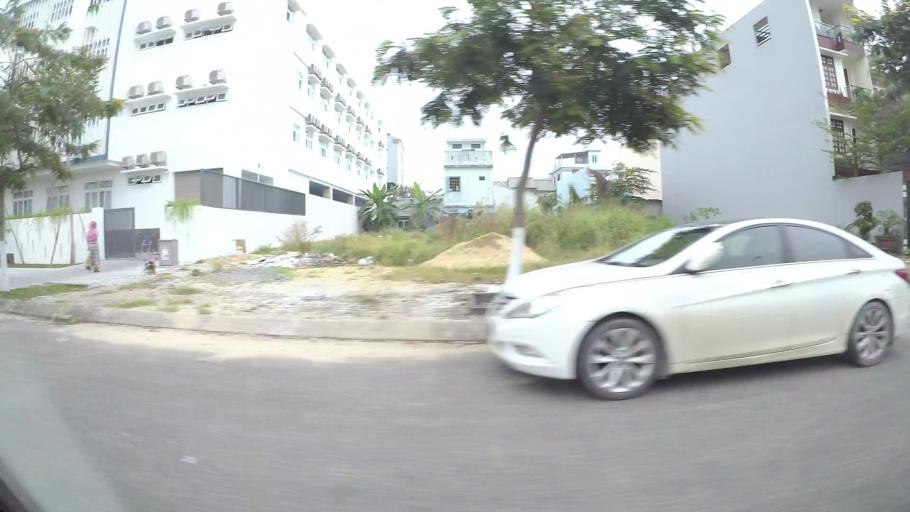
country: VN
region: Da Nang
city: Son Tra
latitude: 16.0323
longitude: 108.2293
